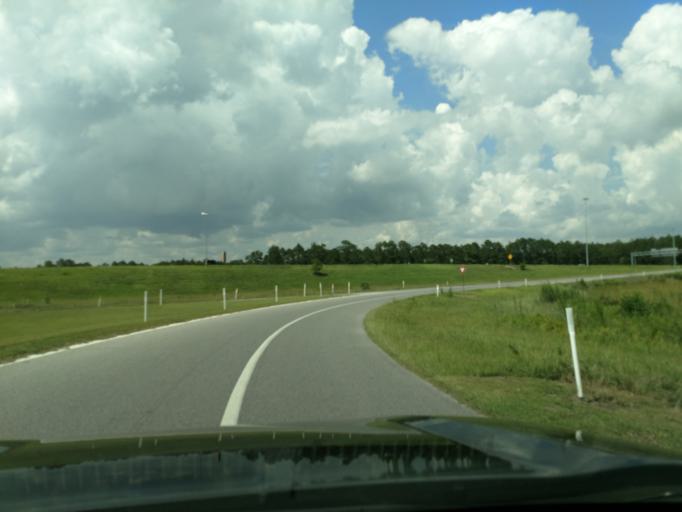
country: US
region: Mississippi
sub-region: Jackson County
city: Gulf Hills
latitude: 30.4527
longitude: -88.8422
